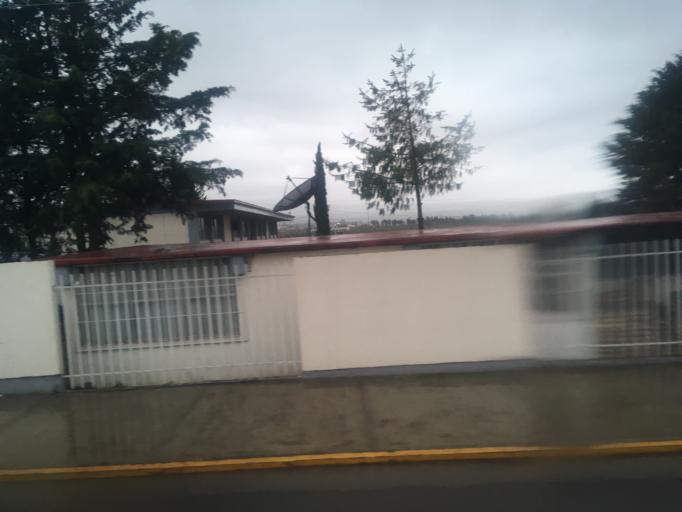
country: MX
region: Puebla
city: Chignahuapan
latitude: 19.8475
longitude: -98.0275
